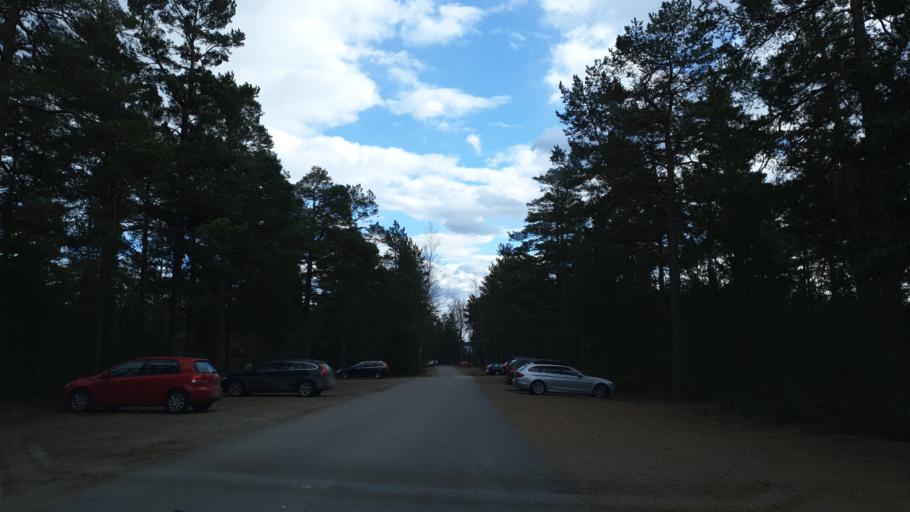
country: SE
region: Stockholm
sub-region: Varmdo Kommun
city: Hemmesta
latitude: 59.2184
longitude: 18.5240
